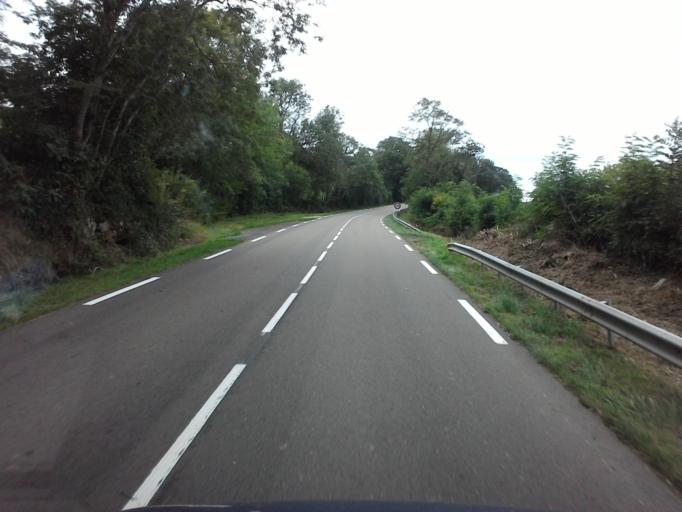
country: FR
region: Bourgogne
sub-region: Departement de Saone-et-Loire
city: Saint-Eusebe
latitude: 46.6306
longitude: 4.4656
